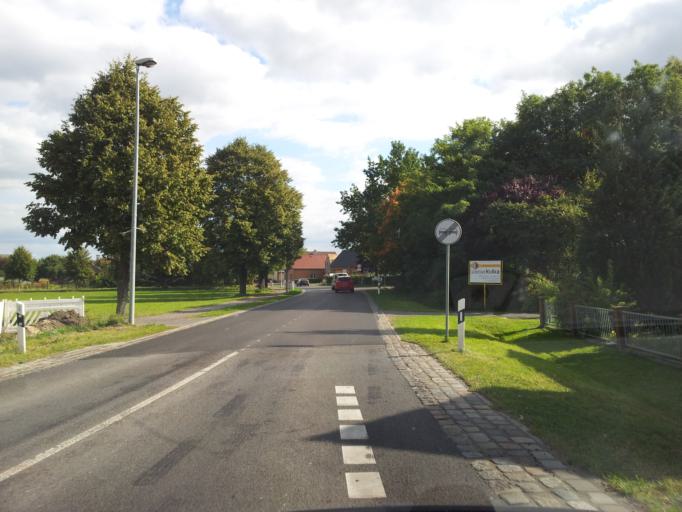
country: DE
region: Brandenburg
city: Sallgast
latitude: 51.5934
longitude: 13.9214
